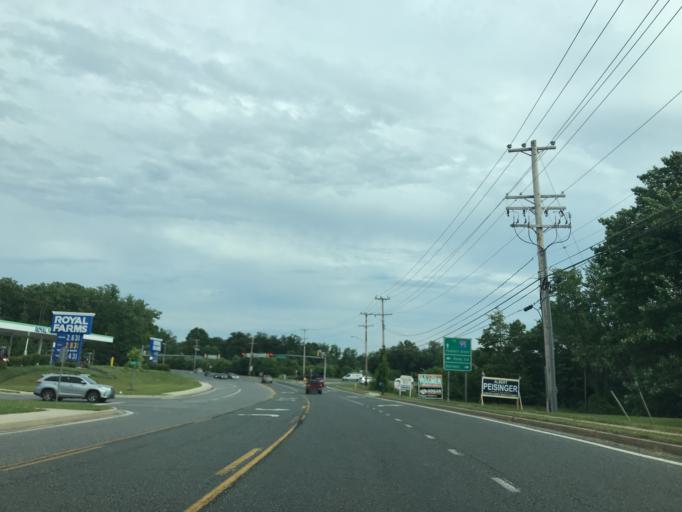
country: US
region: Maryland
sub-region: Harford County
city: Bel Air North
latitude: 39.5765
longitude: -76.3441
